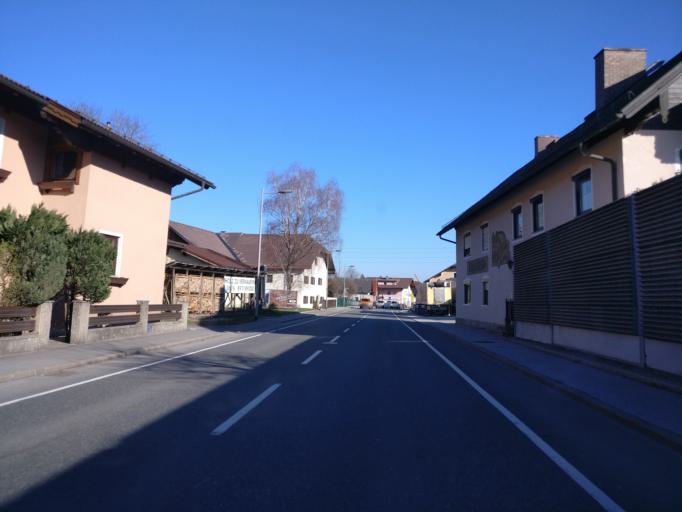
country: AT
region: Salzburg
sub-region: Politischer Bezirk Hallein
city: Oberalm
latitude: 47.6967
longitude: 13.1004
